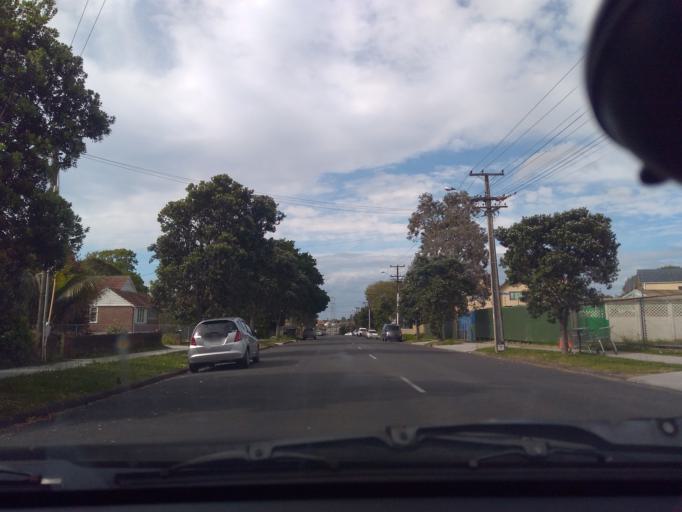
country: NZ
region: Auckland
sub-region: Auckland
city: Waitakere
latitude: -36.9058
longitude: 174.6835
